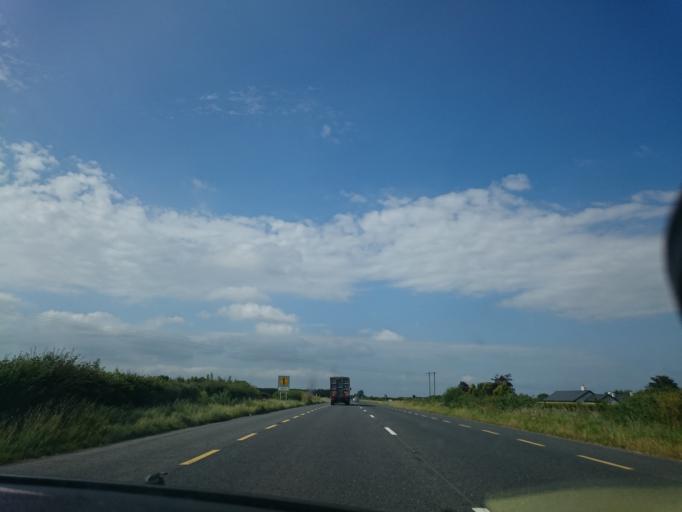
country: IE
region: Leinster
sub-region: Kilkenny
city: Kilkenny
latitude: 52.6012
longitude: -7.2422
